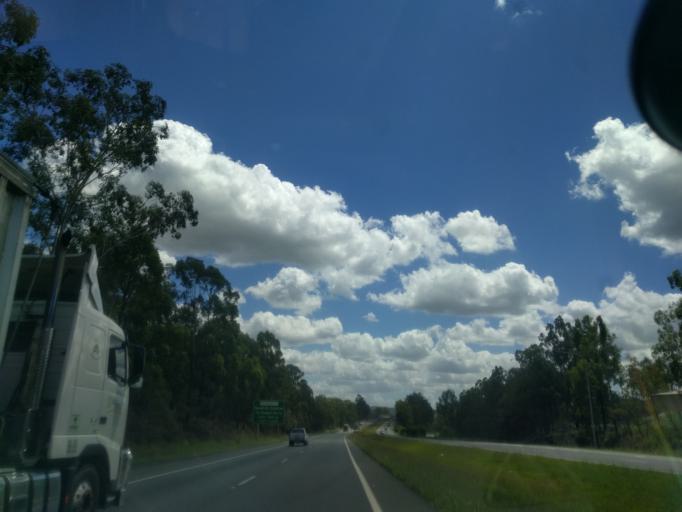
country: AU
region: Queensland
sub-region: Ipswich
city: Bundamba
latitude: -27.6066
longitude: 152.8300
